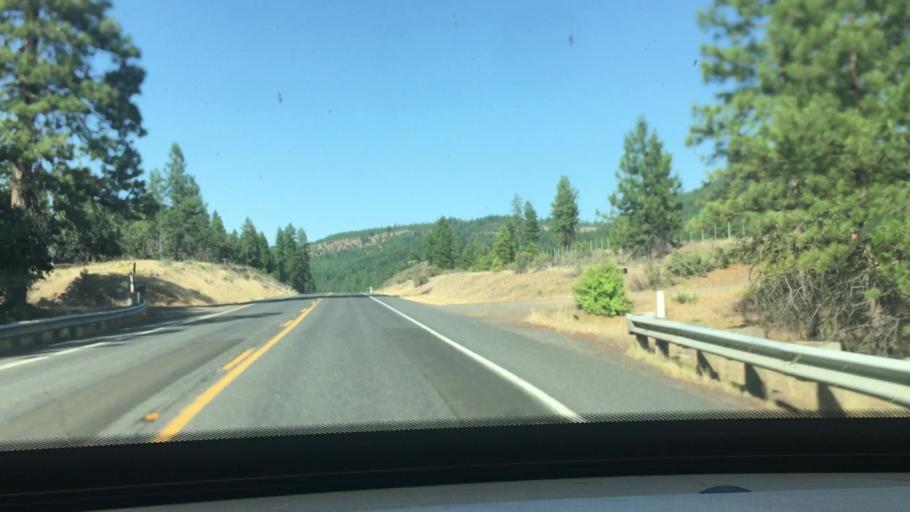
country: US
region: Washington
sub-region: Klickitat County
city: Goldendale
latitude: 45.9446
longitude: -120.6748
